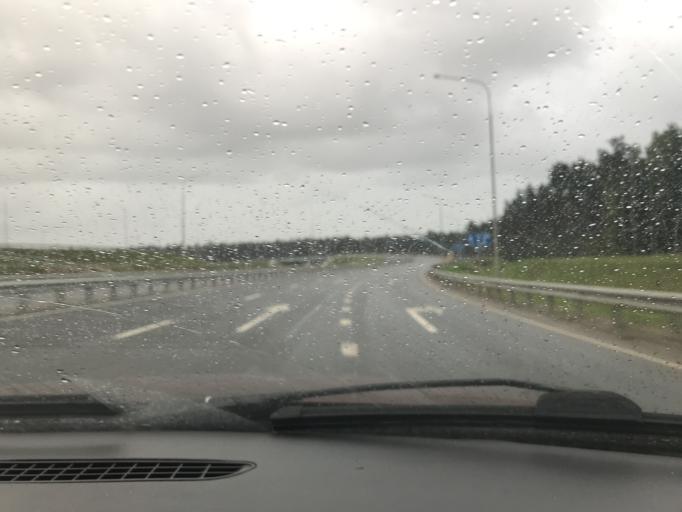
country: RU
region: Kaluga
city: Mstikhino
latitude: 54.5873
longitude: 36.0691
